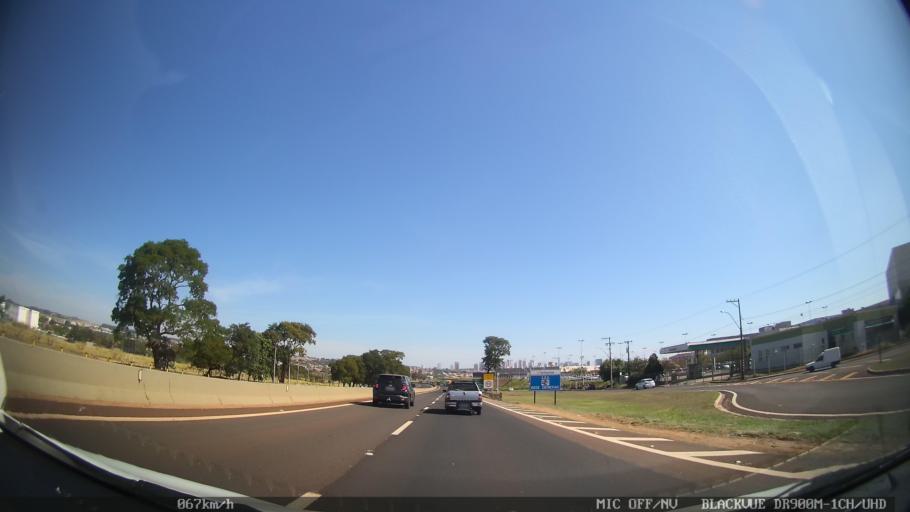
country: BR
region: Sao Paulo
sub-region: Ribeirao Preto
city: Ribeirao Preto
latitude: -21.2088
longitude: -47.7657
